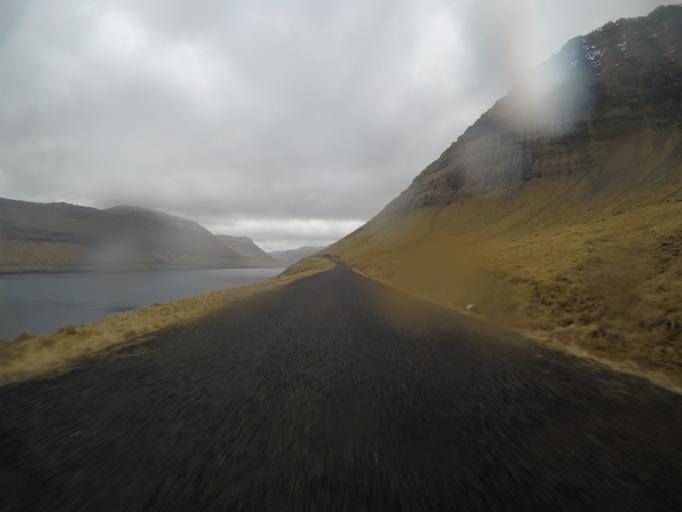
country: FO
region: Nordoyar
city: Klaksvik
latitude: 62.3341
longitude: -6.5762
